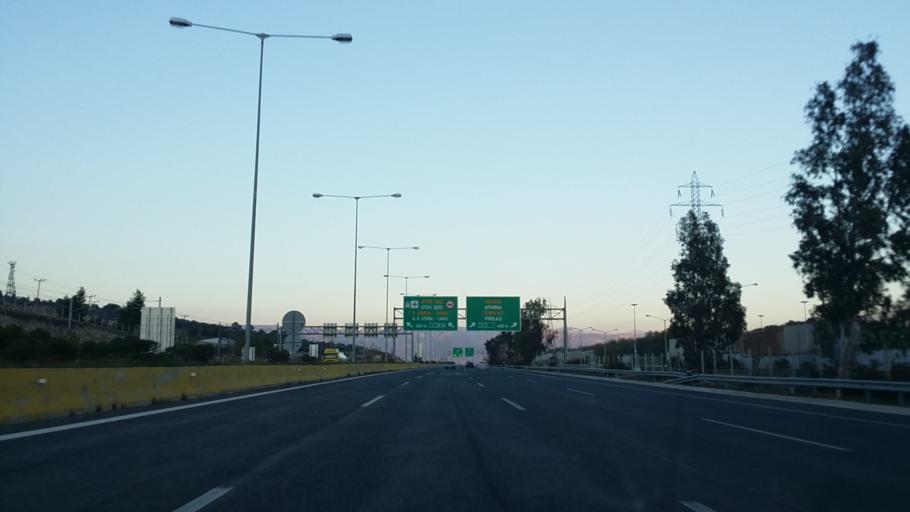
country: GR
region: Attica
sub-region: Nomarchia Dytikis Attikis
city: Mandra
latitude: 38.0467
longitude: 23.4999
